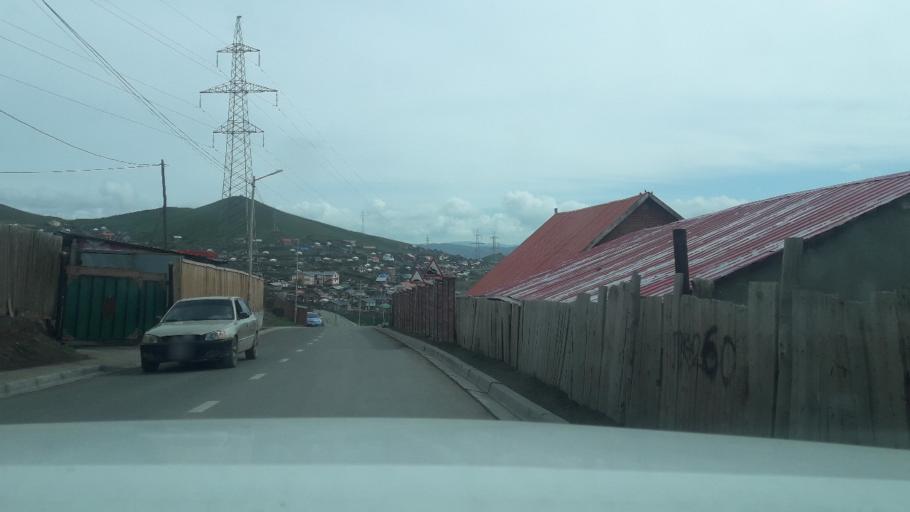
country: MN
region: Ulaanbaatar
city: Ulaanbaatar
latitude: 47.9663
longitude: 106.8816
